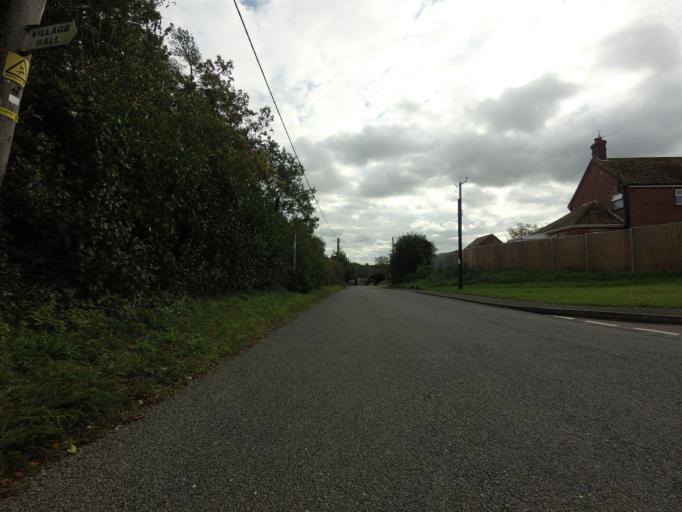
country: GB
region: England
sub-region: Norfolk
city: Snettisham
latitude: 52.9017
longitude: 0.5438
